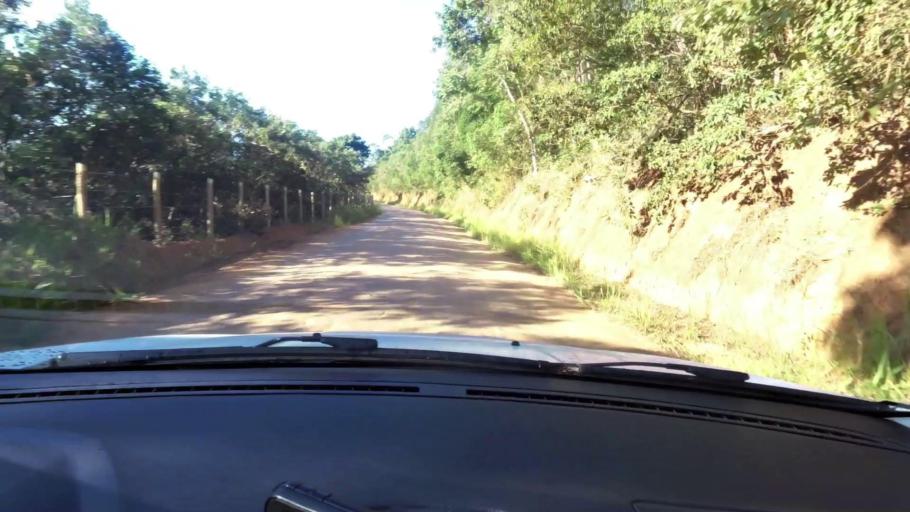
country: BR
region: Espirito Santo
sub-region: Guarapari
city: Guarapari
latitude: -20.7274
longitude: -40.5895
